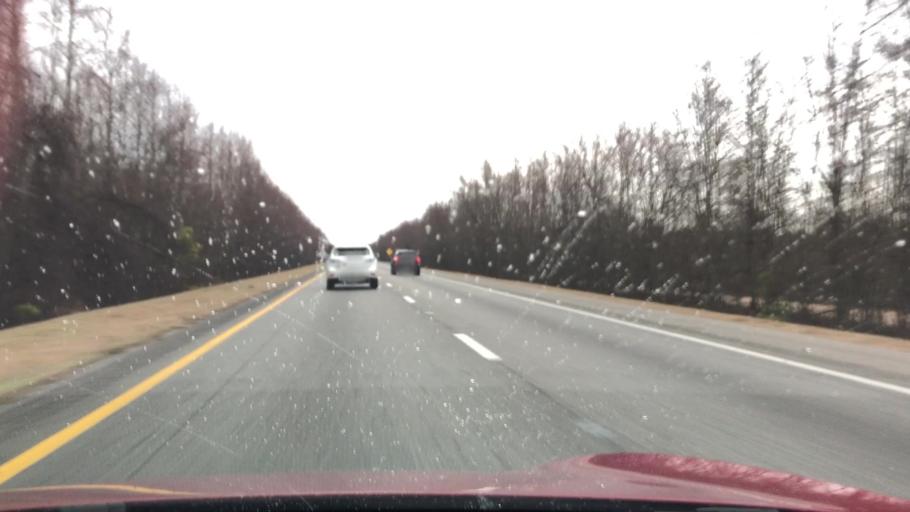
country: US
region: South Carolina
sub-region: Dillon County
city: Latta
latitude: 34.3251
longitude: -79.5762
